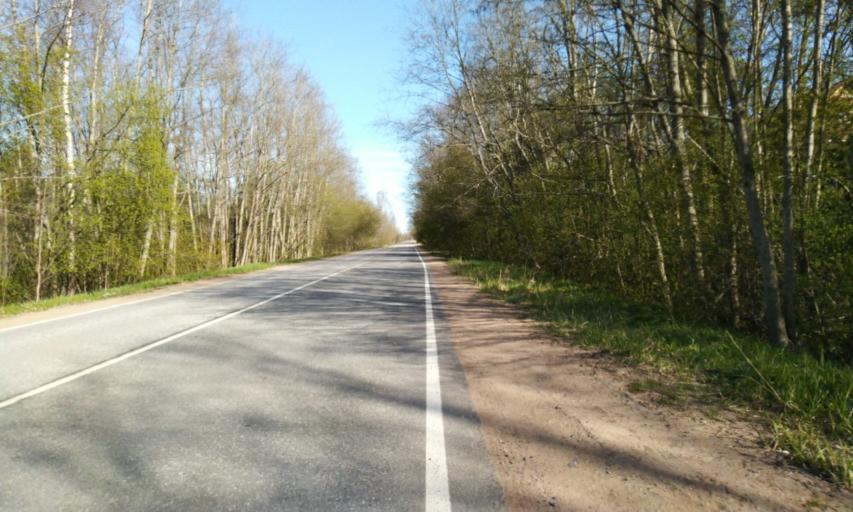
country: RU
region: Leningrad
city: Leskolovo
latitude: 60.3255
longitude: 30.4272
